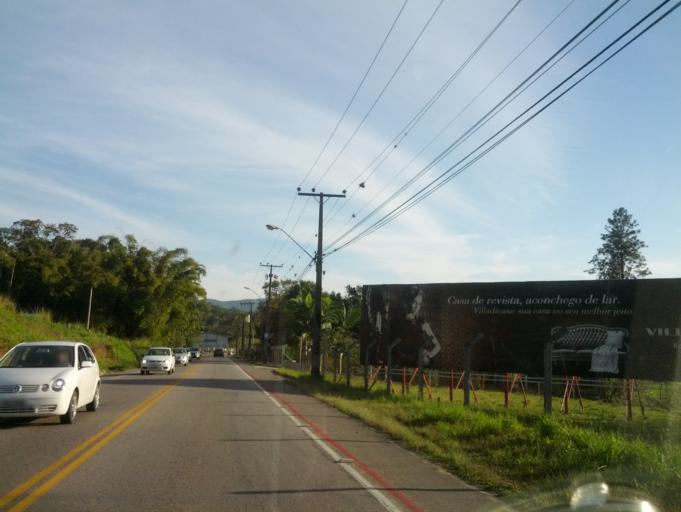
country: BR
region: Santa Catarina
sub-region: Indaial
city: Indaial
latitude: -26.8812
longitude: -49.1772
